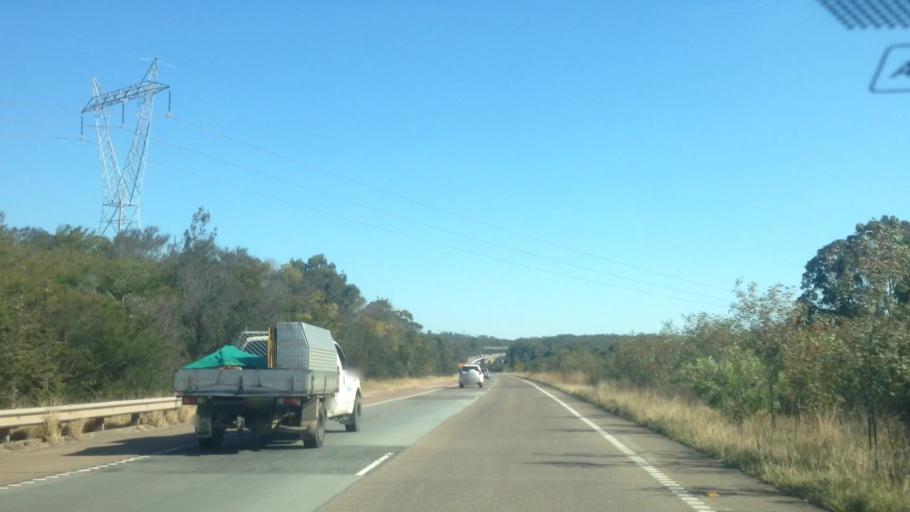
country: AU
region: New South Wales
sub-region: Wyong Shire
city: Jilliby
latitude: -33.2065
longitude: 151.4567
